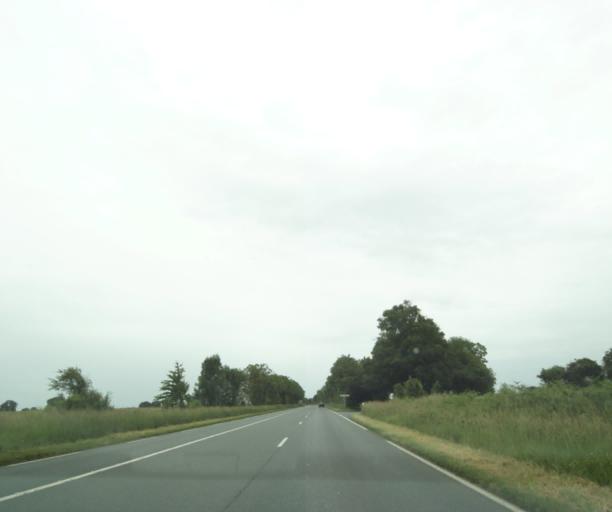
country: FR
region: Poitou-Charentes
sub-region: Departement des Deux-Sevres
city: Cherveux
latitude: 46.4274
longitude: -0.3941
